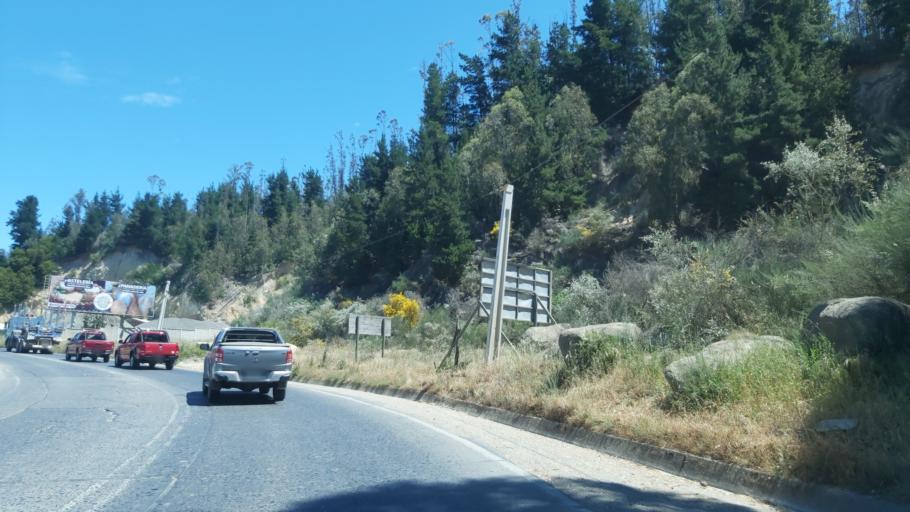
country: CL
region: Maule
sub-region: Provincia de Talca
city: Constitucion
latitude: -35.3473
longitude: -72.4137
